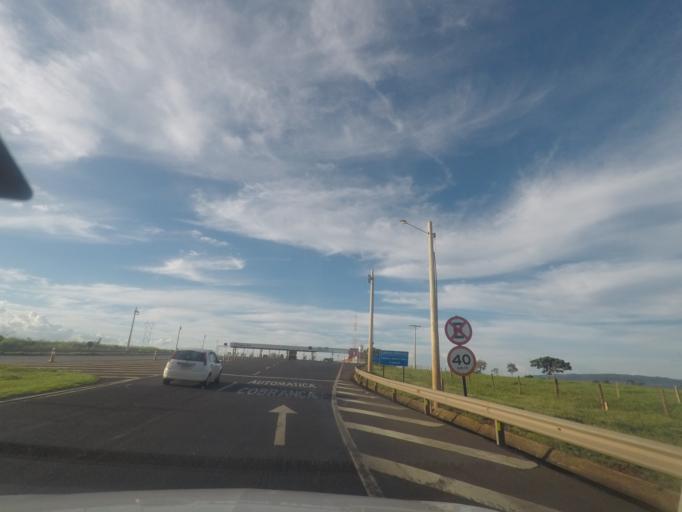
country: BR
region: Goias
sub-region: Itumbiara
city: Itumbiara
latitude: -18.2704
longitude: -49.2452
